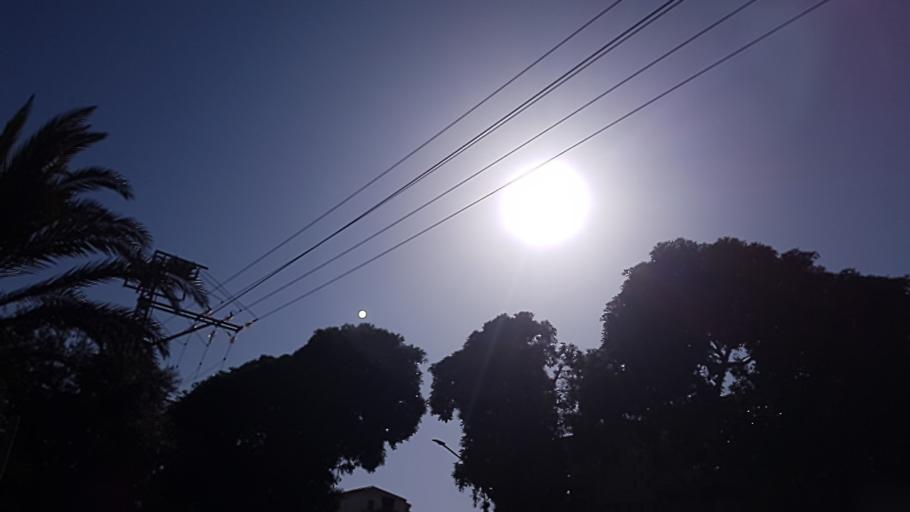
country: IL
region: Tel Aviv
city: Giv`atayim
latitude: 32.0705
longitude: 34.8227
